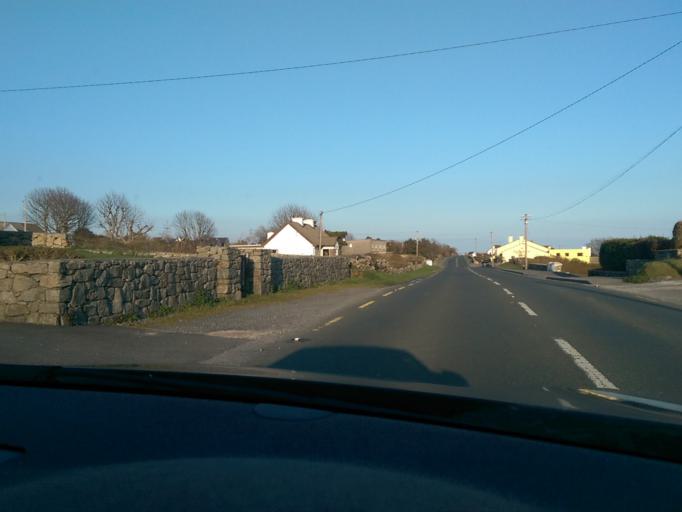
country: IE
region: Connaught
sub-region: County Galway
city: Oughterard
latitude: 53.2450
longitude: -9.3551
